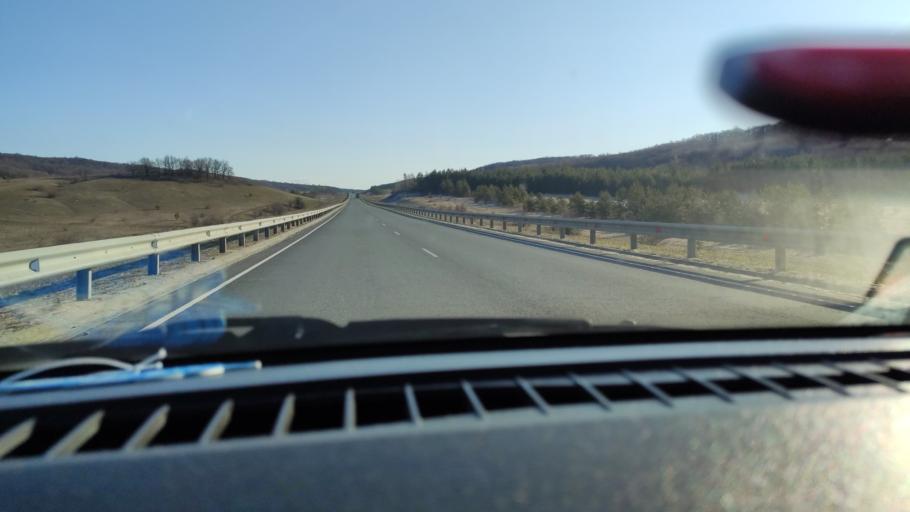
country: RU
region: Saratov
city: Alekseyevka
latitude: 52.4000
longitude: 47.9890
